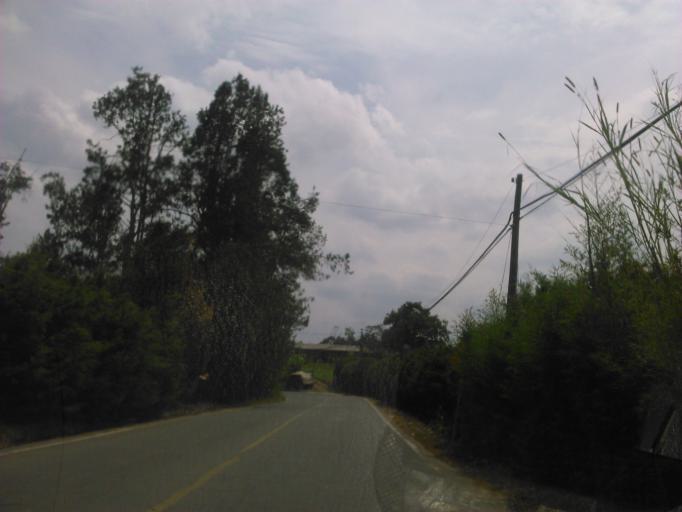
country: CO
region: Antioquia
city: San Vicente
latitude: 6.2389
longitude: -75.3749
